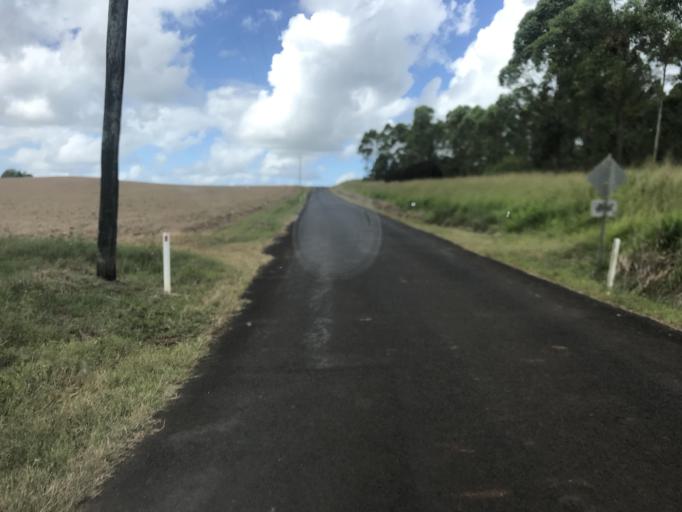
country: AU
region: Queensland
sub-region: Cassowary Coast
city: Innisfail
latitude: -17.5529
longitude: 145.8830
